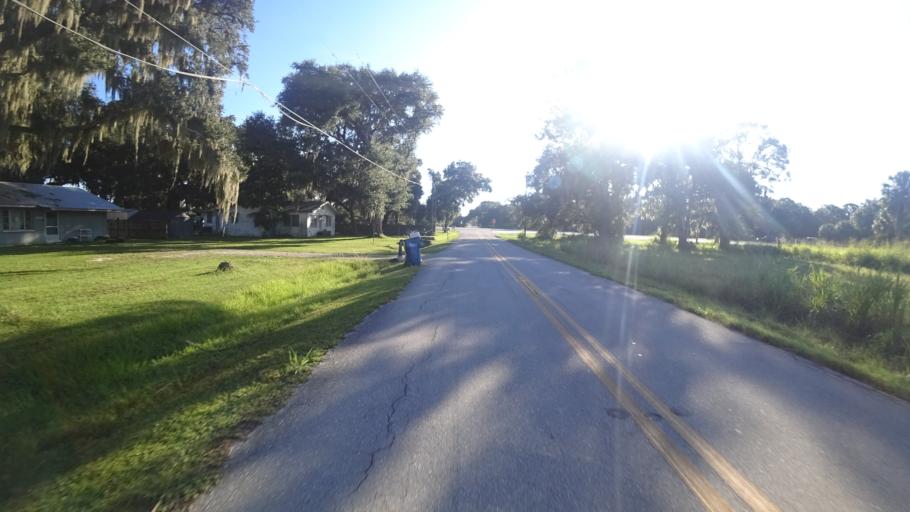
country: US
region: Florida
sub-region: Manatee County
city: Memphis
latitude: 27.5683
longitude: -82.5468
